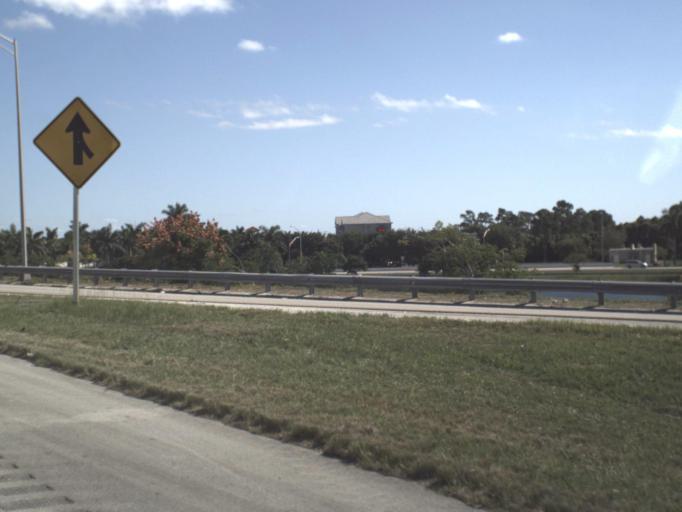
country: US
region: Florida
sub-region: Miami-Dade County
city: Leisure City
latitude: 25.4766
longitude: -80.4408
